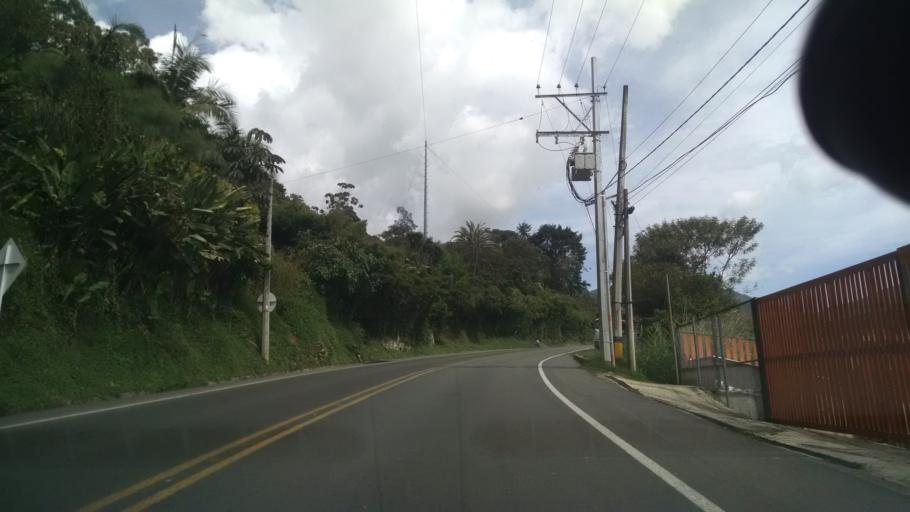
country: CO
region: Antioquia
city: Caldas
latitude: 6.0403
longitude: -75.6287
